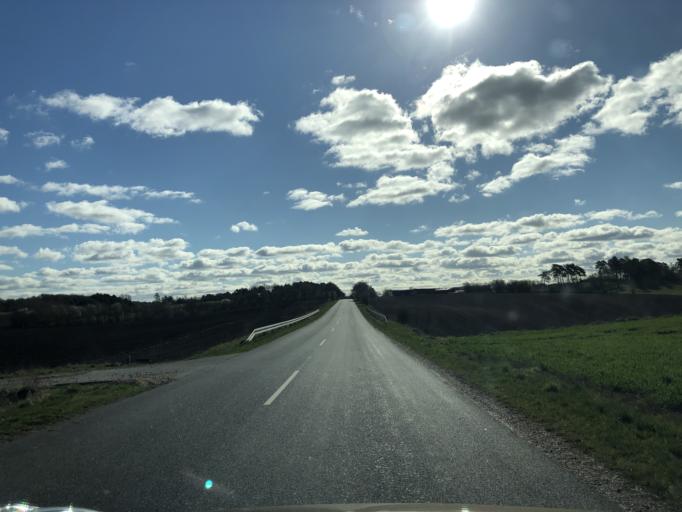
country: DK
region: North Denmark
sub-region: Vesthimmerland Kommune
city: Alestrup
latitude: 56.6142
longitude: 9.5224
